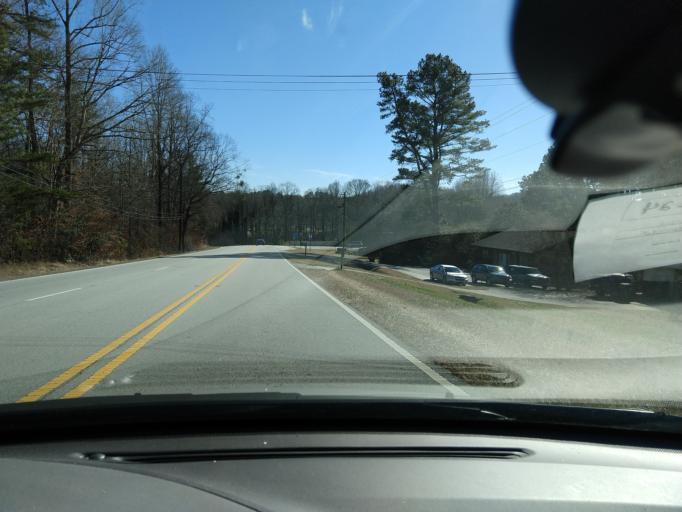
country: US
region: Georgia
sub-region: Stephens County
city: Toccoa
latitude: 34.5965
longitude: -83.3484
